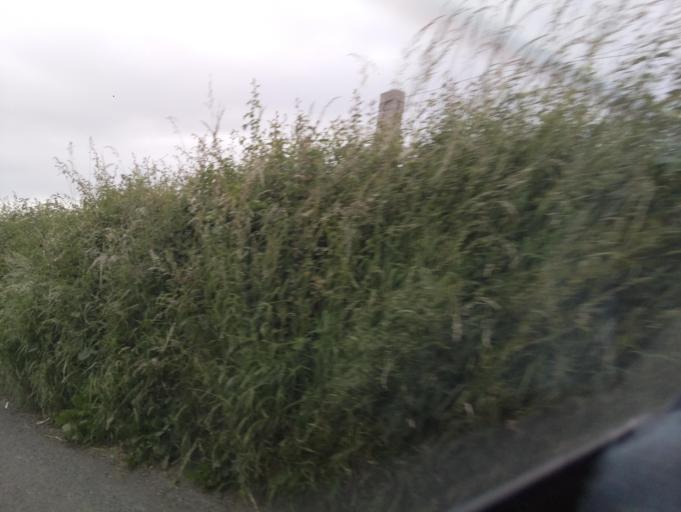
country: GB
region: England
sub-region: Derbyshire
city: Rodsley
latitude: 52.8804
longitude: -1.7498
